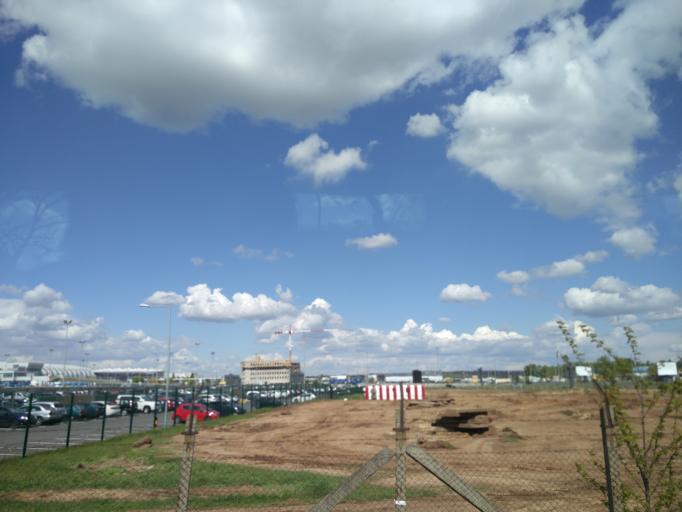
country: HU
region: Pest
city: Vecses
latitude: 47.4269
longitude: 19.2598
